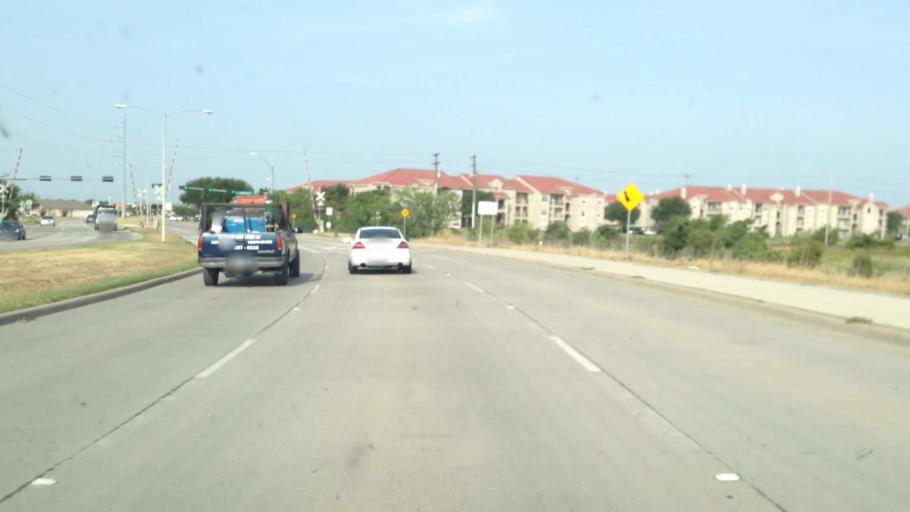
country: US
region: Texas
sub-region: Denton County
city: Lewisville
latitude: 33.0143
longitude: -96.9604
